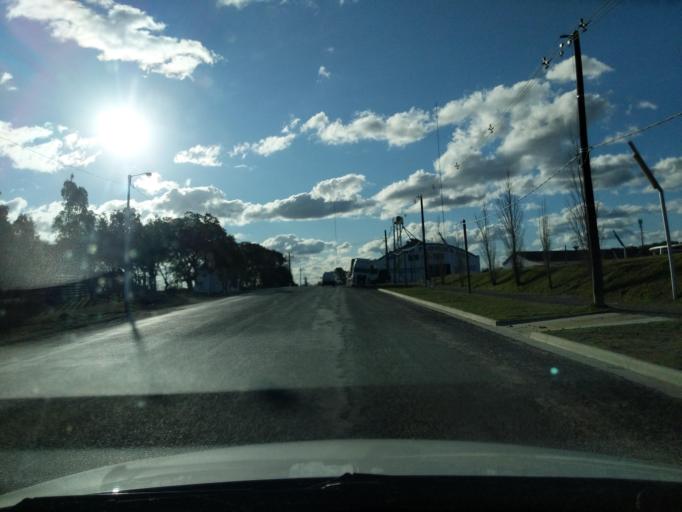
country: UY
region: Florida
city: Florida
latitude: -34.1000
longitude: -56.2321
